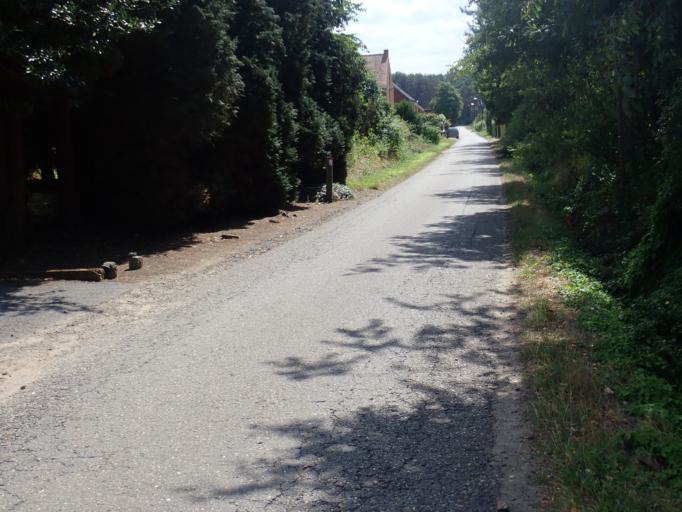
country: BE
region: Flanders
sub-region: Provincie Antwerpen
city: Herselt
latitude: 51.0538
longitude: 4.9180
